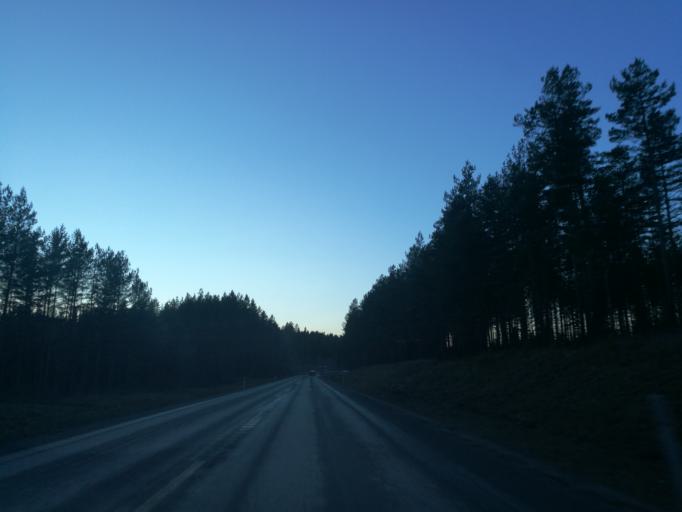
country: NO
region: Hedmark
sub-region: Eidskog
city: Skotterud
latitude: 59.9372
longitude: 12.2054
